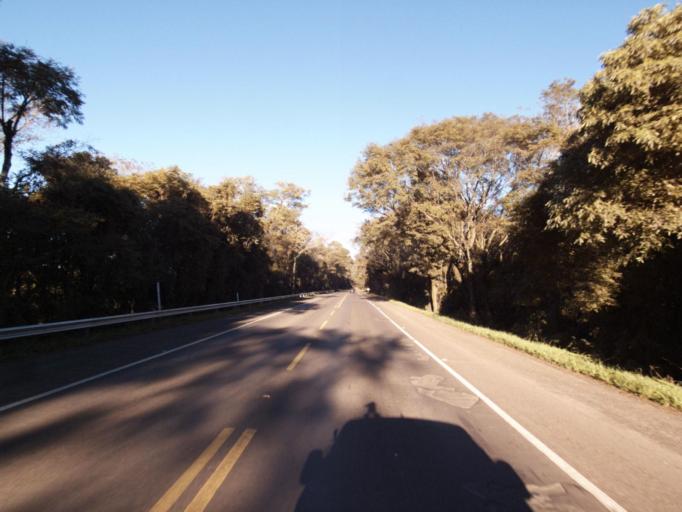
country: BR
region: Santa Catarina
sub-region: Sao Lourenco Do Oeste
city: Sao Lourenco dOeste
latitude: -26.7675
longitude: -53.2605
